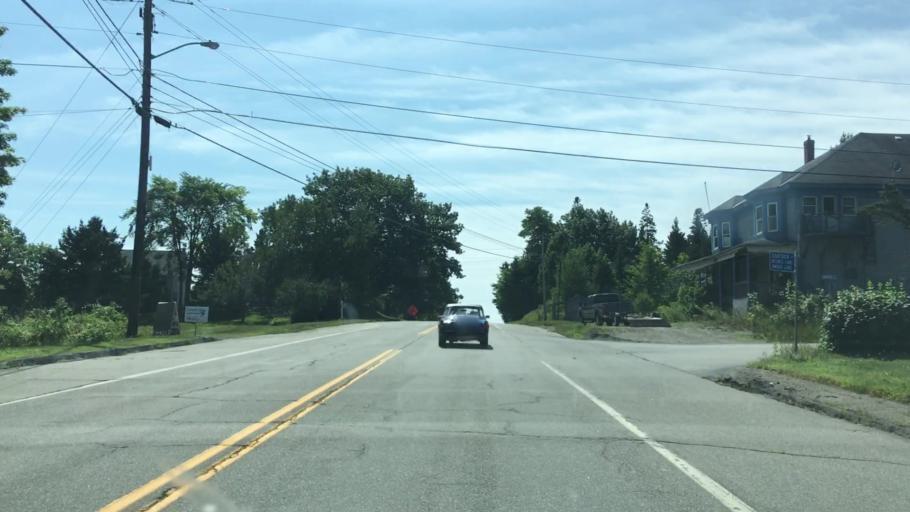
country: CA
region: New Brunswick
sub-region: Charlotte County
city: Saint Andrews
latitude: 45.1206
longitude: -67.1458
